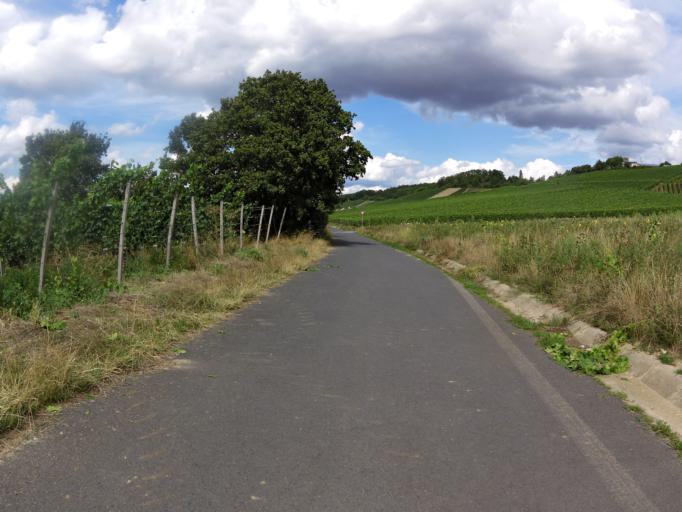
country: DE
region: Bavaria
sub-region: Regierungsbezirk Unterfranken
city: Sommerhausen
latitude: 49.6963
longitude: 10.0303
